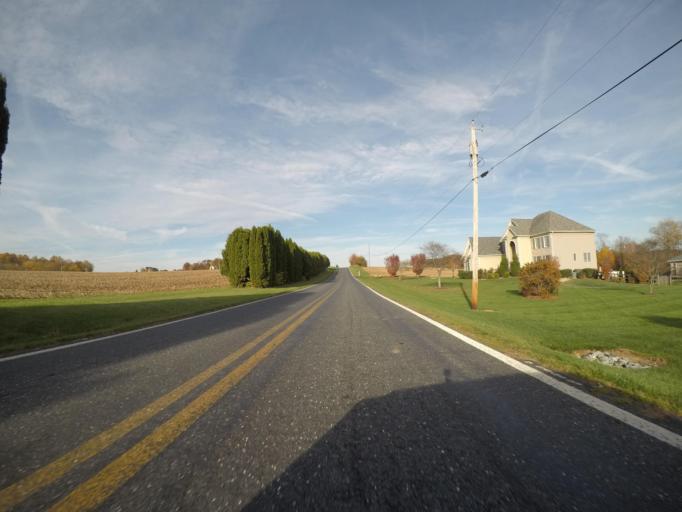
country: US
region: Maryland
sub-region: Carroll County
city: Hampstead
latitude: 39.5618
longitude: -76.9083
